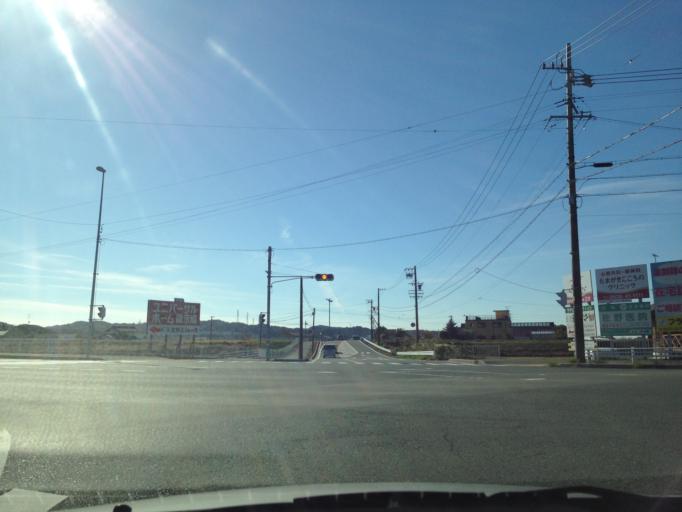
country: JP
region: Shizuoka
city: Kakegawa
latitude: 34.7601
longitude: 137.9720
